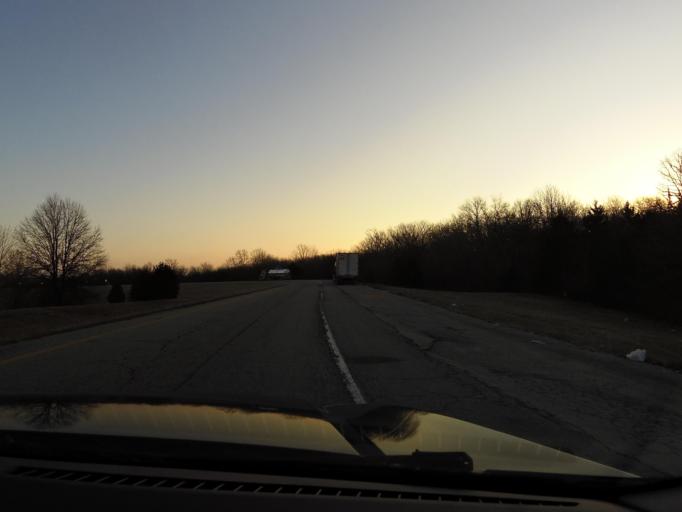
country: US
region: Illinois
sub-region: Marion County
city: Salem
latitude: 38.7573
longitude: -88.8935
